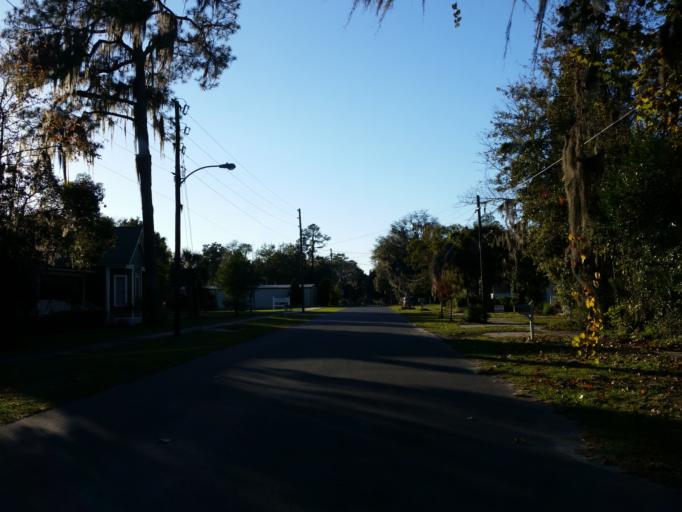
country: US
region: Florida
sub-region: Hamilton County
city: Jasper
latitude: 30.5209
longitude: -82.9526
